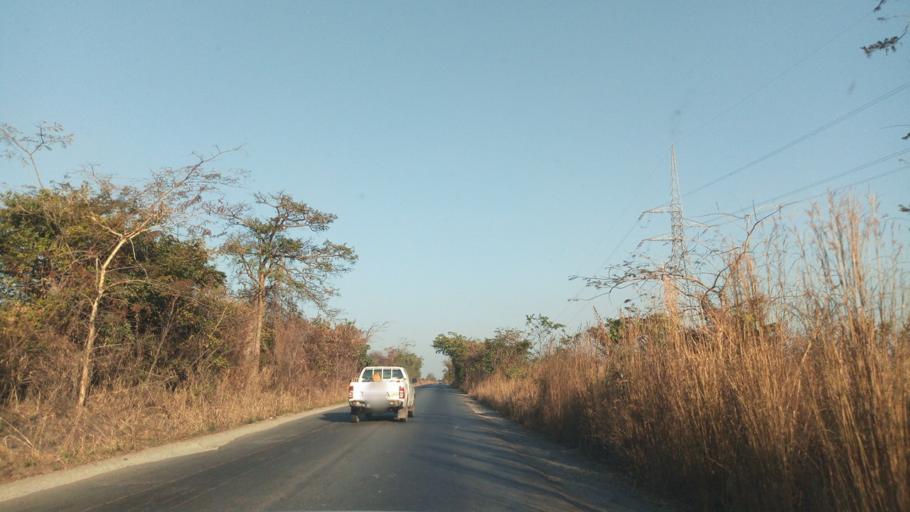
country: CD
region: Katanga
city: Likasi
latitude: -11.1045
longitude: 27.0167
